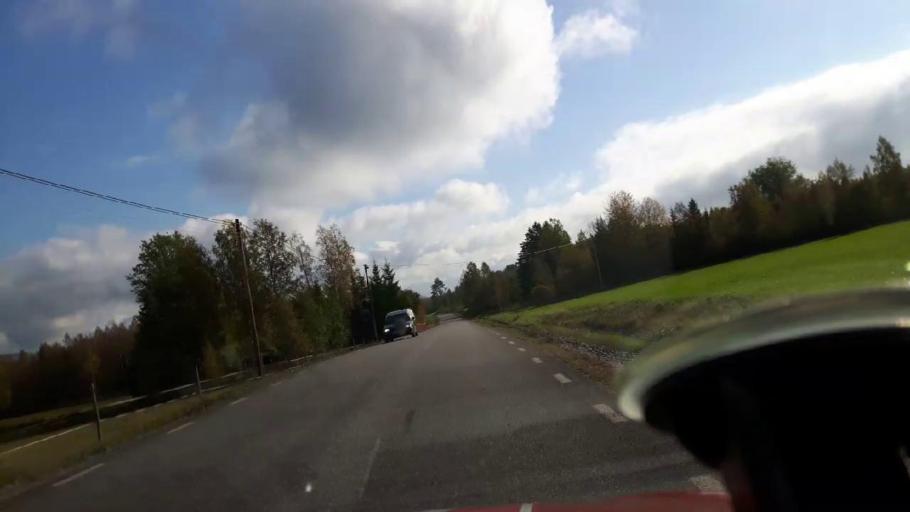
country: SE
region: Gaevleborg
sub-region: Ljusdals Kommun
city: Ljusdal
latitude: 61.7588
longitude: 16.0992
